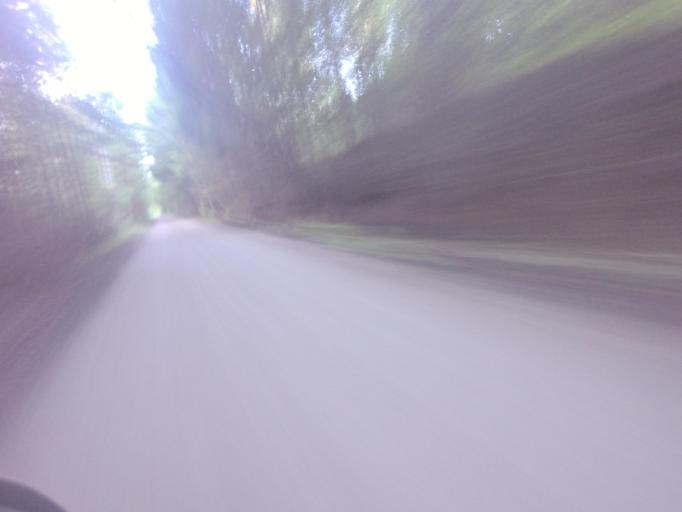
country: CA
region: Ontario
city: Bradford West Gwillimbury
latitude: 44.0014
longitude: -79.8060
